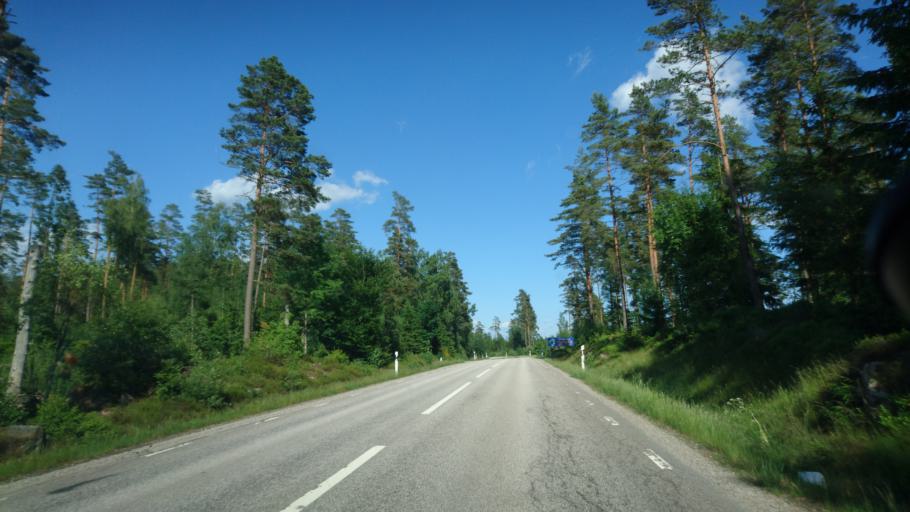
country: SE
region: Skane
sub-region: Osby Kommun
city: Lonsboda
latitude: 56.3908
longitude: 14.4269
